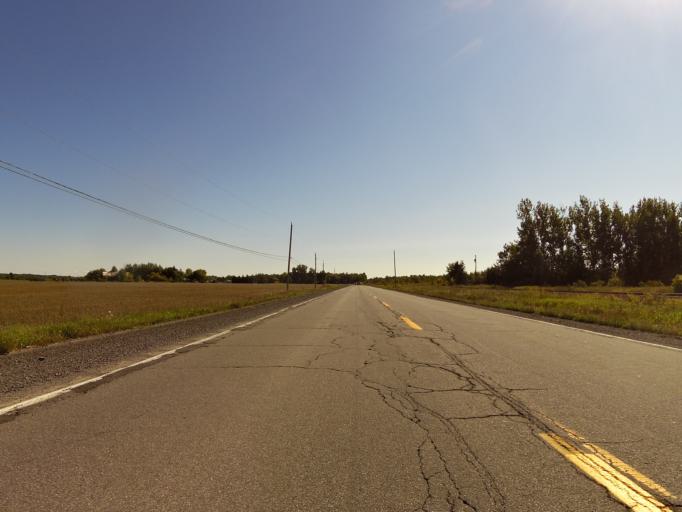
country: CA
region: Ontario
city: Clarence-Rockland
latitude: 45.3632
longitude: -75.4231
